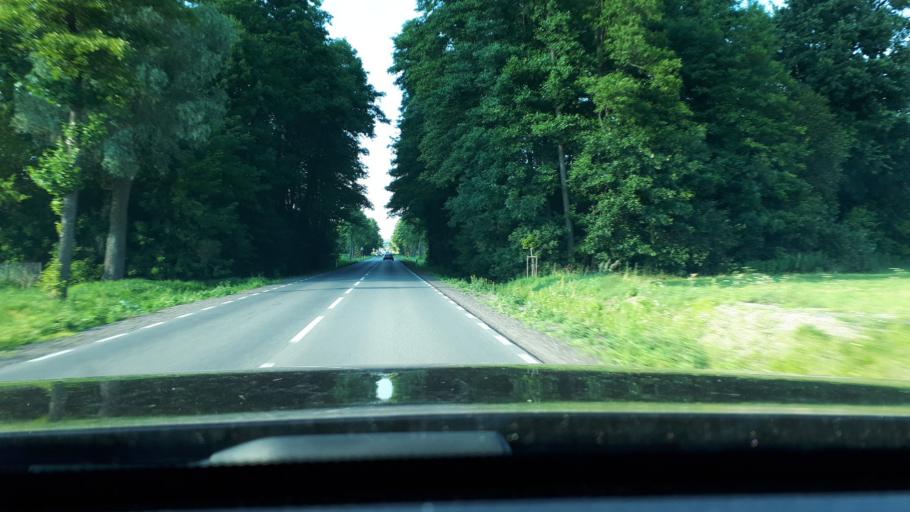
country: PL
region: Masovian Voivodeship
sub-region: Powiat ciechanowski
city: Ojrzen
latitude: 52.7539
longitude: 20.5350
